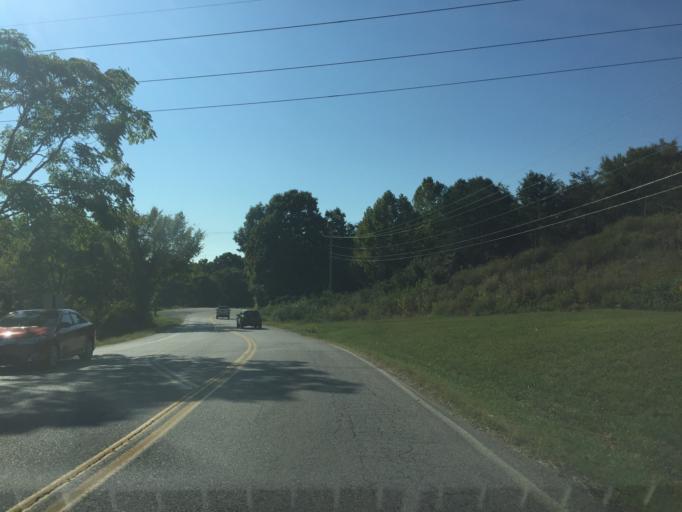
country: US
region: Tennessee
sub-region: Hamilton County
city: Harrison
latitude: 35.1044
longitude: -85.1595
